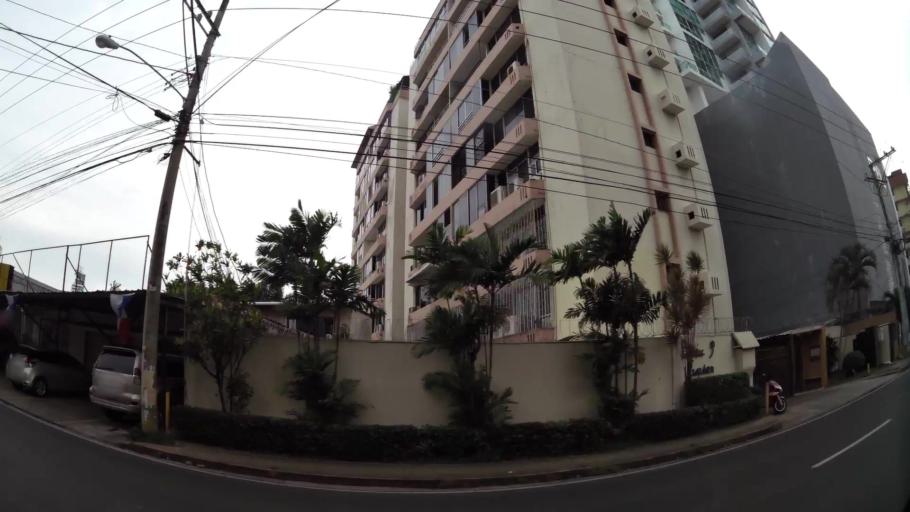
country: PA
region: Panama
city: Panama
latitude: 8.9963
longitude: -79.5032
